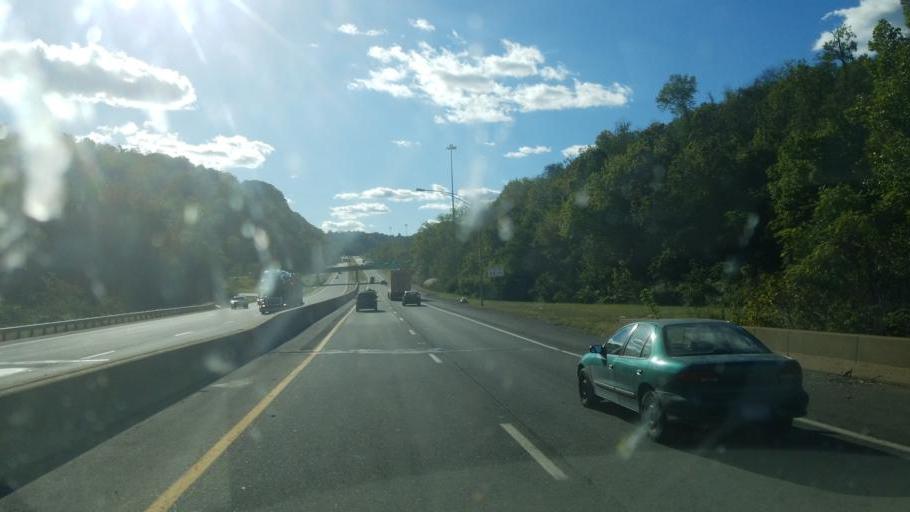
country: US
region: West Virginia
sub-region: Ohio County
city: Wheeling
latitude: 40.0494
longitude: -80.7339
